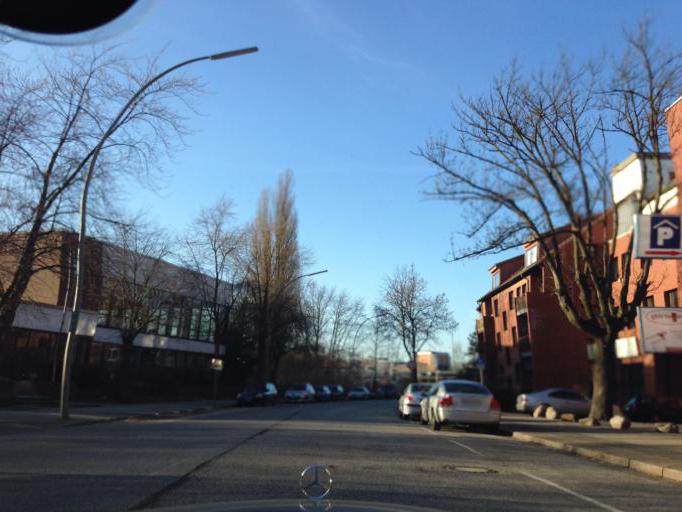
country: DE
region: Hamburg
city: Marienthal
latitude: 53.5754
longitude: 10.0738
